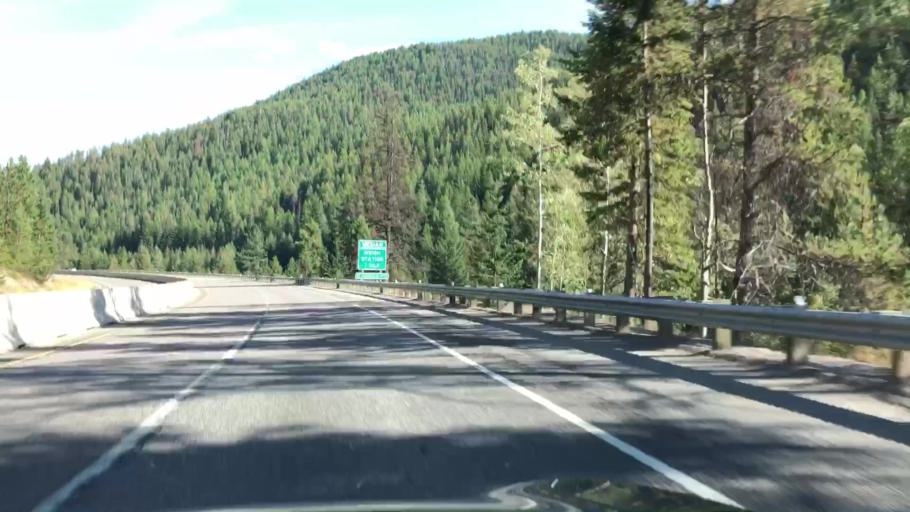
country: US
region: Montana
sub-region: Sanders County
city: Thompson Falls
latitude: 47.3952
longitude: -115.4538
